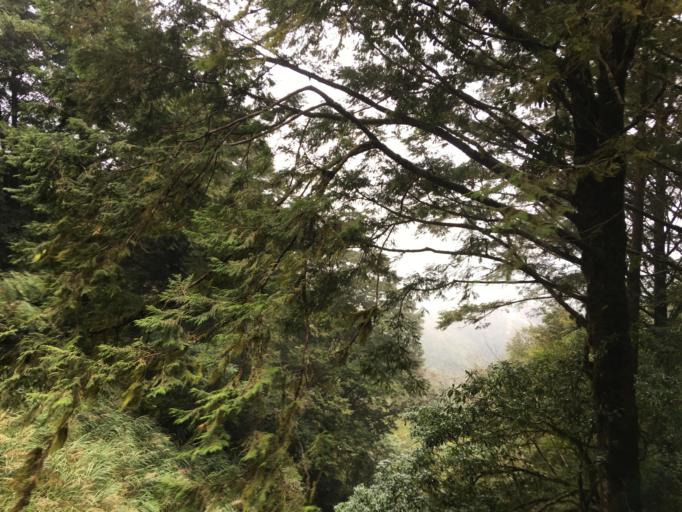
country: TW
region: Taiwan
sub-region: Yilan
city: Yilan
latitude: 24.4854
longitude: 121.5341
